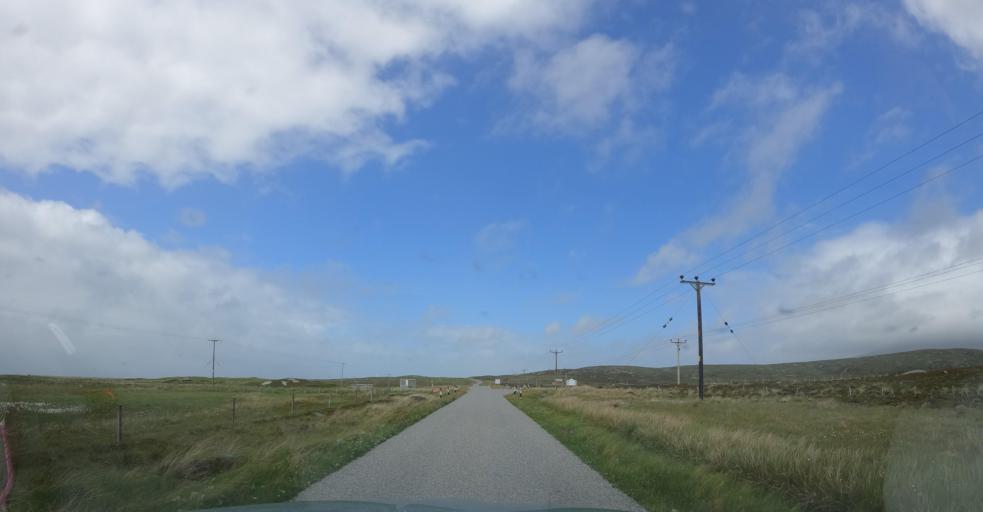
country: GB
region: Scotland
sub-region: Eilean Siar
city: Isle of South Uist
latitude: 57.2246
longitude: -7.3935
